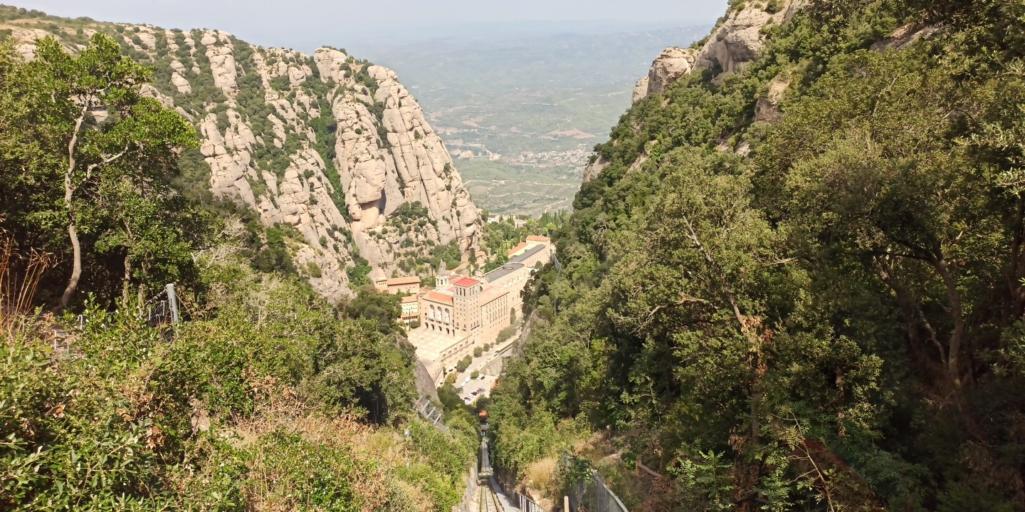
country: ES
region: Catalonia
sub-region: Provincia de Barcelona
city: Collbato
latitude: 41.5889
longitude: 1.8335
